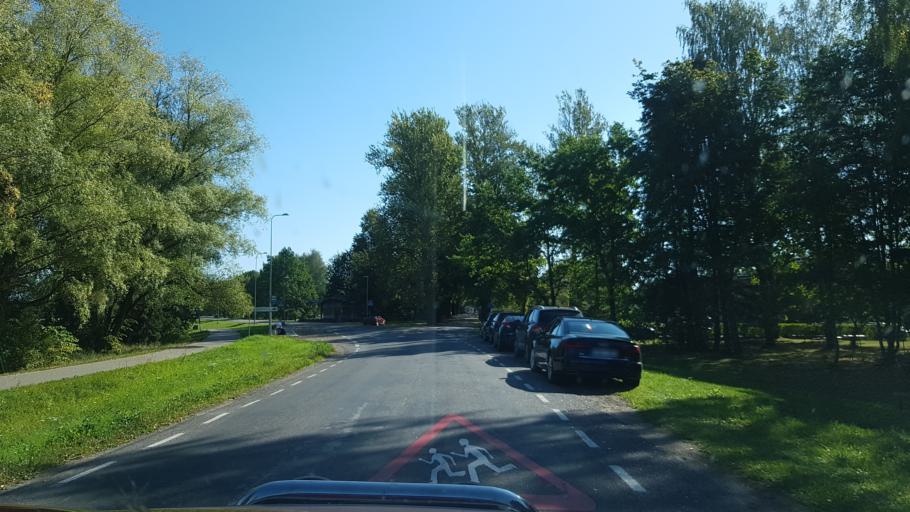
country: EE
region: Tartu
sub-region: Tartu linn
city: Tartu
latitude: 58.3564
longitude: 26.8715
